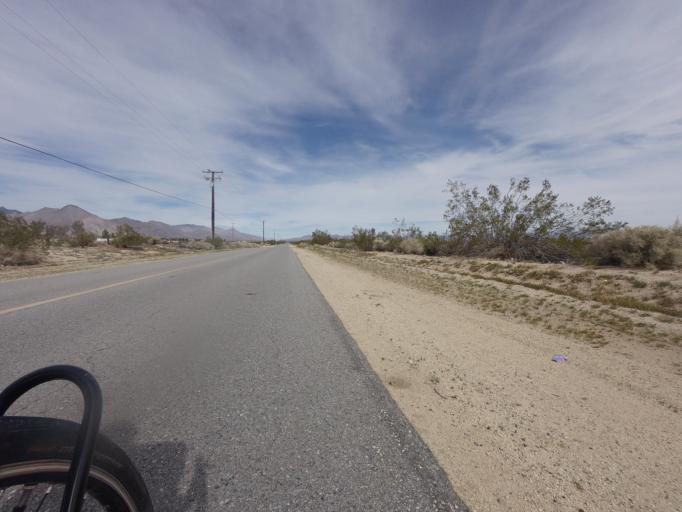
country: US
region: California
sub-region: Kern County
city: Inyokern
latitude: 35.7313
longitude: -117.8374
